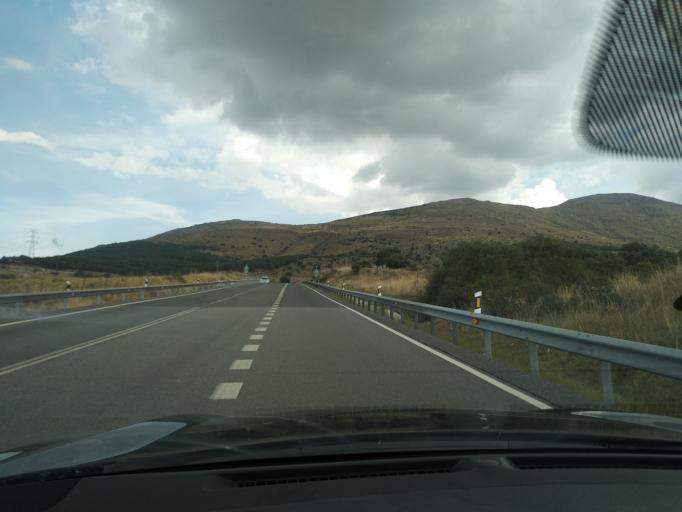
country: ES
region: Castille and Leon
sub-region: Provincia de Segovia
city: Otero de Herreros
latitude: 40.7672
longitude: -4.2027
